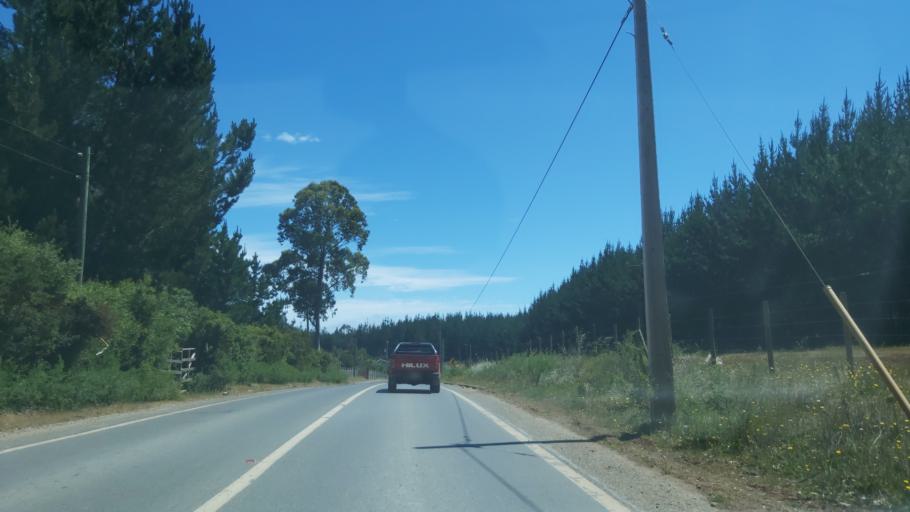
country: CL
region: Maule
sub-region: Provincia de Talca
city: Constitucion
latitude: -35.3977
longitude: -72.4325
